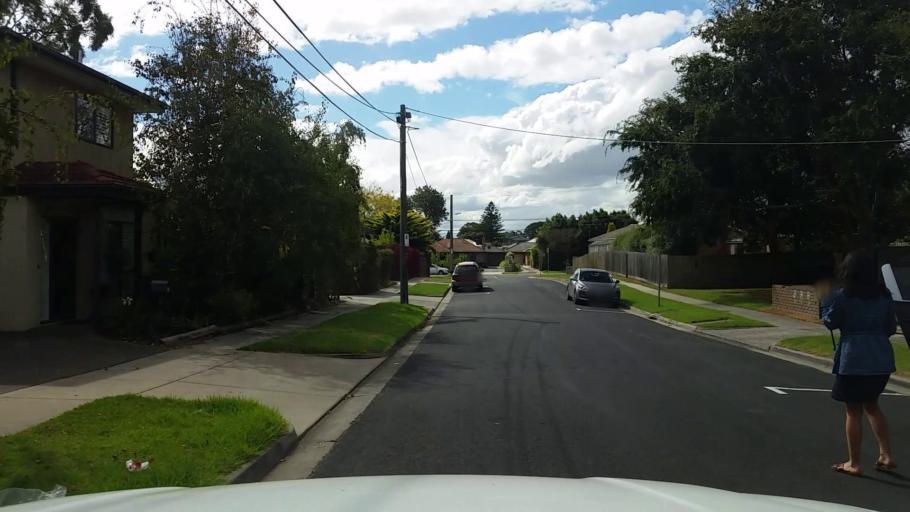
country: AU
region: Victoria
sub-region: Frankston
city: Frankston East
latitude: -38.1465
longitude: 145.1398
